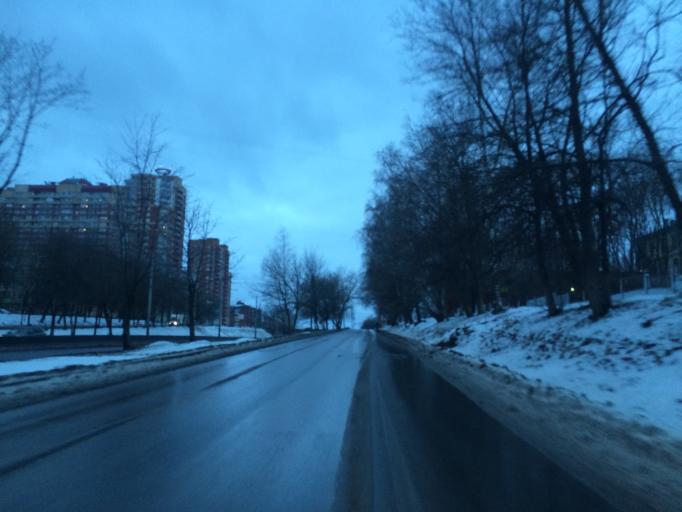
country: RU
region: Tula
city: Mendeleyevskiy
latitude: 54.1564
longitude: 37.5890
